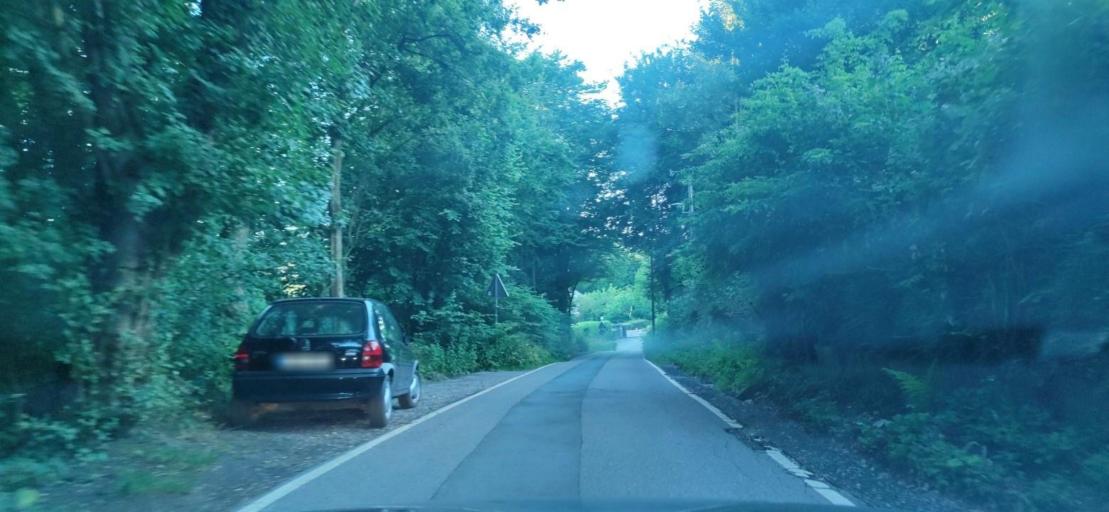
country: DE
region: North Rhine-Westphalia
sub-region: Regierungsbezirk Dusseldorf
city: Velbert
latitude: 51.3945
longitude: 7.0741
